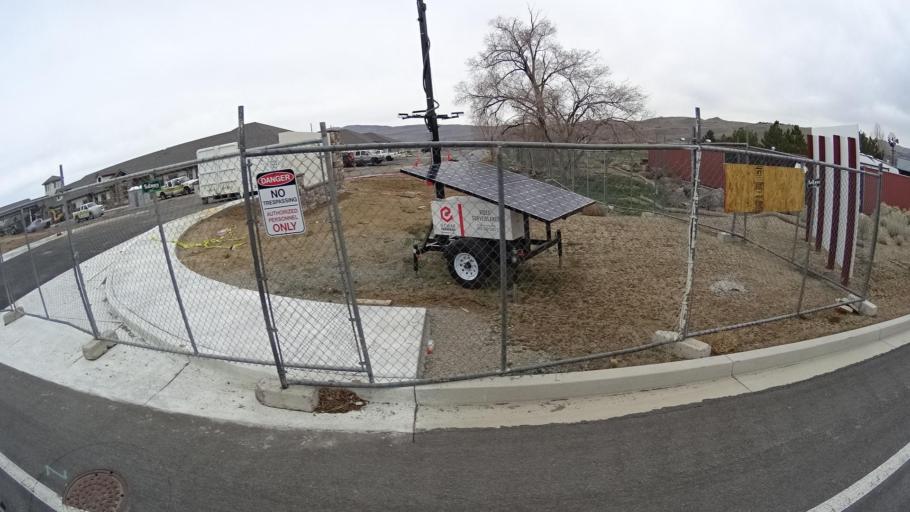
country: US
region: Nevada
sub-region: Washoe County
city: Spanish Springs
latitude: 39.6055
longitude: -119.7274
